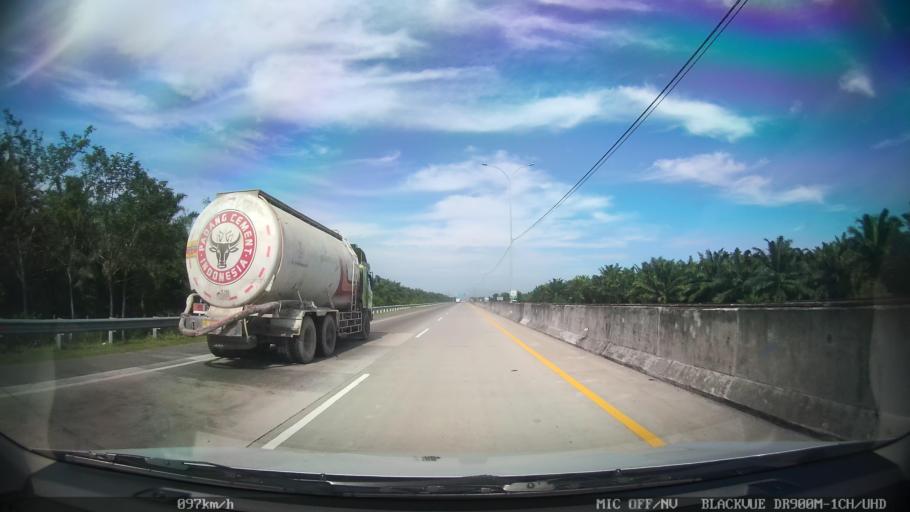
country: ID
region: North Sumatra
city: Sunggal
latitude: 3.6383
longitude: 98.6058
